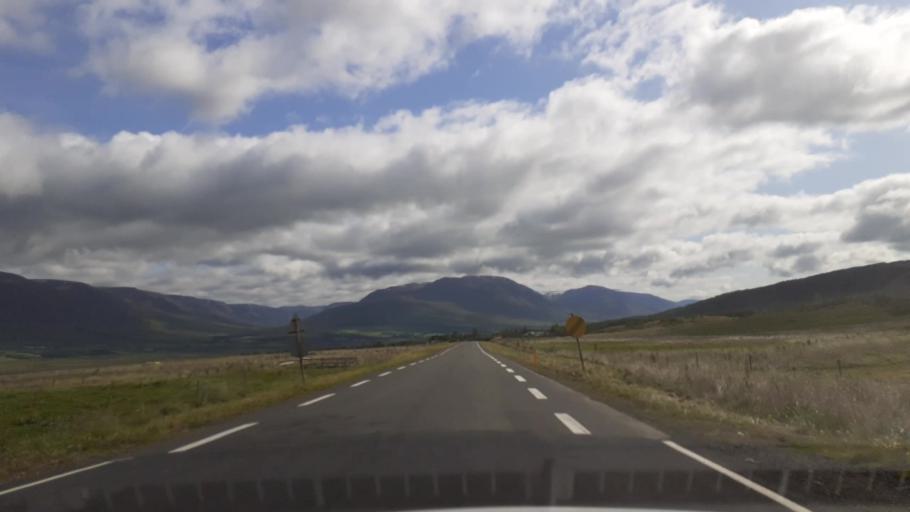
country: IS
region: Northeast
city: Akureyri
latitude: 65.6553
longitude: -18.0961
